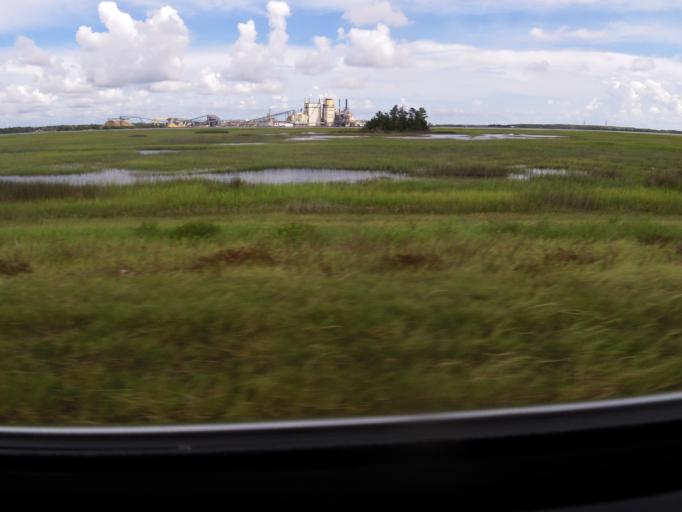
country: US
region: Georgia
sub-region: Glynn County
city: Dock Junction
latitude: 31.1794
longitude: -81.5358
